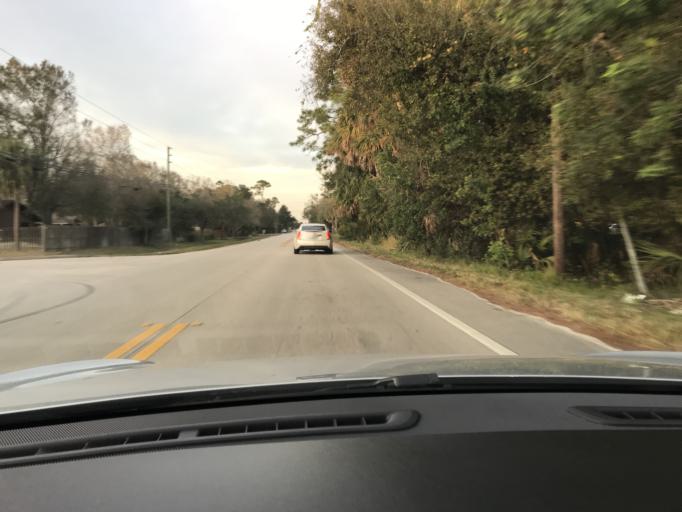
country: US
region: Florida
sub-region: Indian River County
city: Vero Beach South
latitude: 27.6052
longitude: -80.4305
